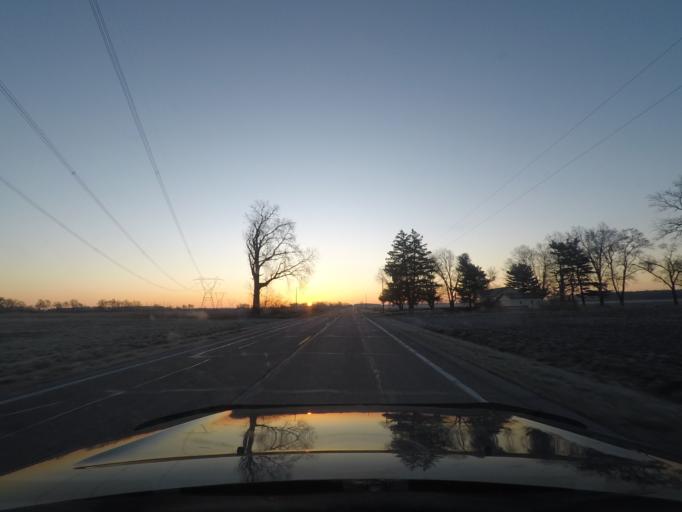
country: US
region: Indiana
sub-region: LaPorte County
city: Fish Lake
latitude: 41.4763
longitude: -86.5830
